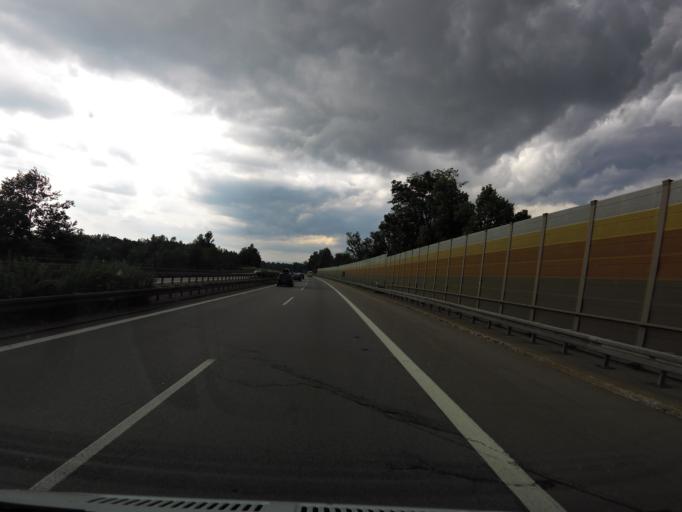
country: DE
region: Bavaria
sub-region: Lower Bavaria
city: Aicha vorm Wald
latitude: 48.6667
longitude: 13.2634
